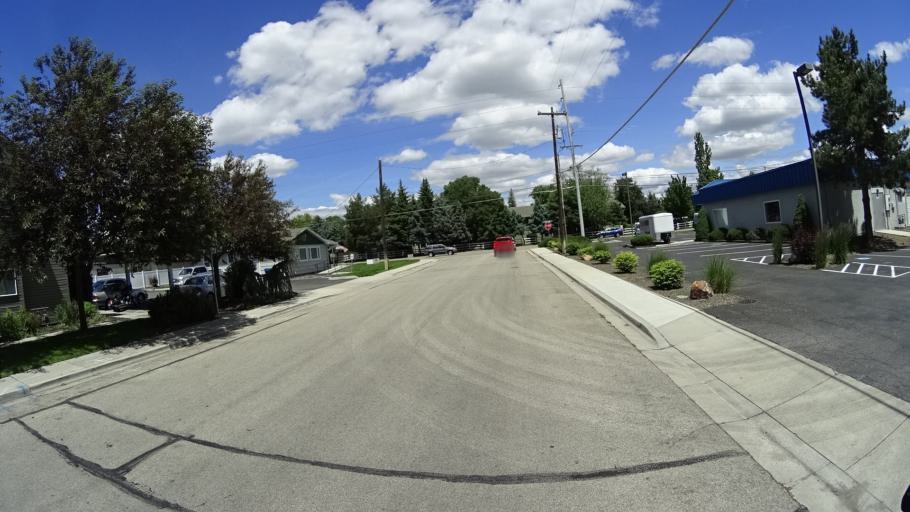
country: US
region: Idaho
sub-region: Ada County
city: Garden City
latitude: 43.5893
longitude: -116.2511
